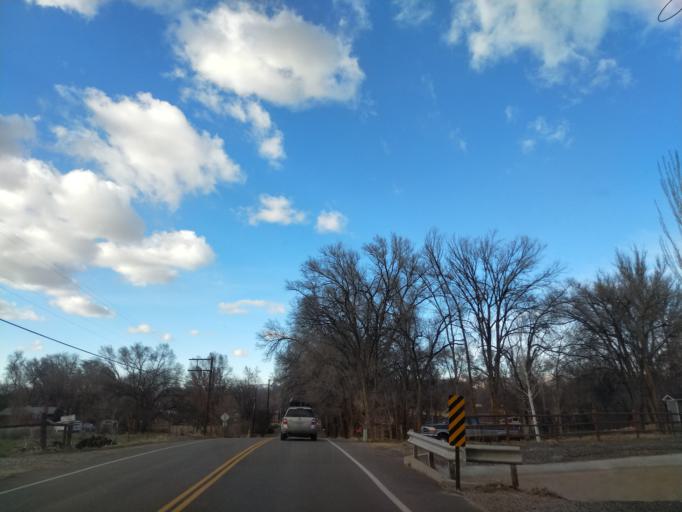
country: US
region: Colorado
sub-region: Mesa County
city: Grand Junction
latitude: 39.0971
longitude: -108.5709
